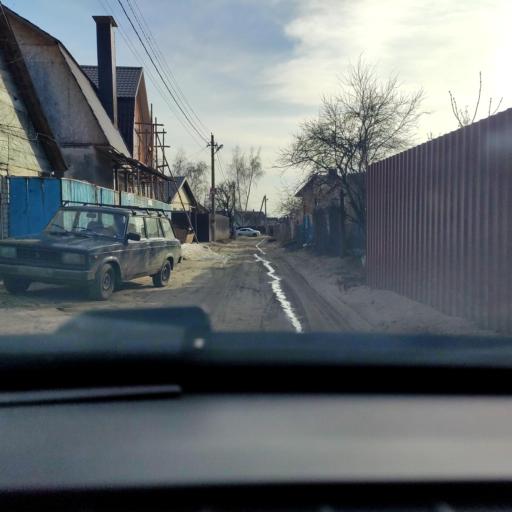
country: RU
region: Voronezj
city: Podgornoye
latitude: 51.7411
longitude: 39.1531
